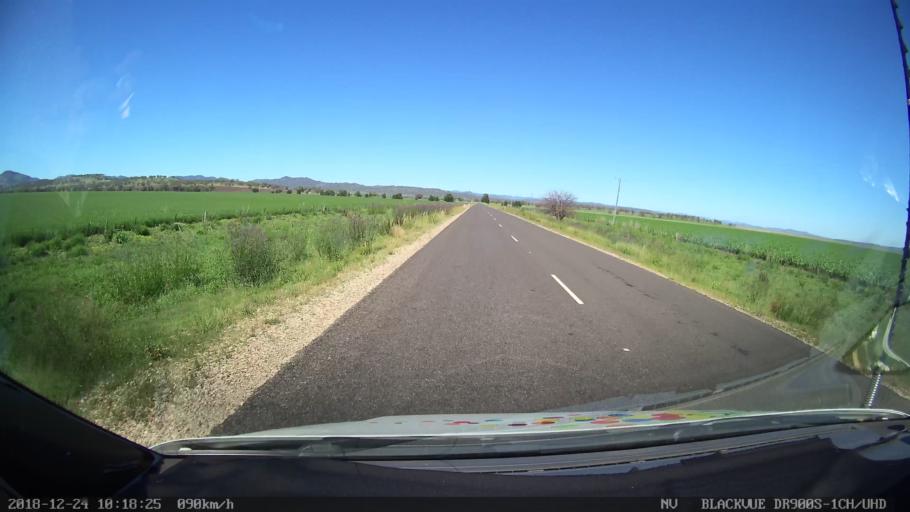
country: AU
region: New South Wales
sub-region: Liverpool Plains
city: Quirindi
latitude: -31.7236
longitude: 150.5770
